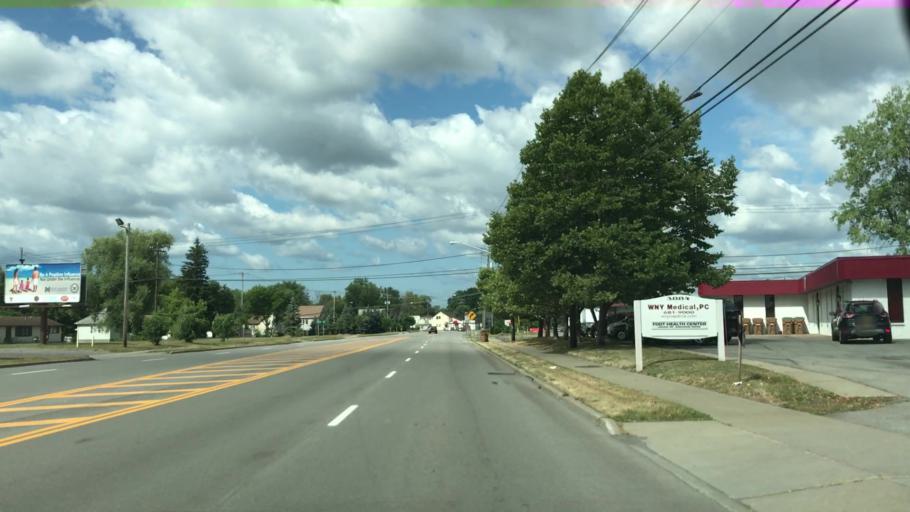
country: US
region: New York
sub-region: Erie County
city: Cheektowaga
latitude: 42.9048
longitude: -78.7300
